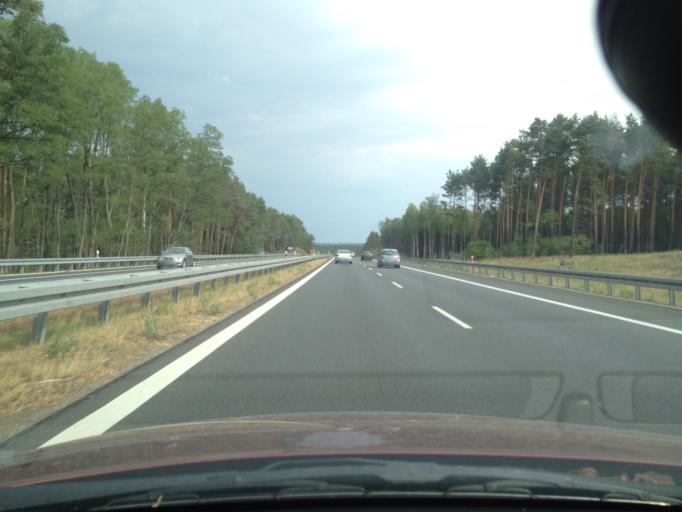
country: PL
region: Lubusz
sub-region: Zielona Gora
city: Zielona Gora
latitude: 51.9724
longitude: 15.5662
